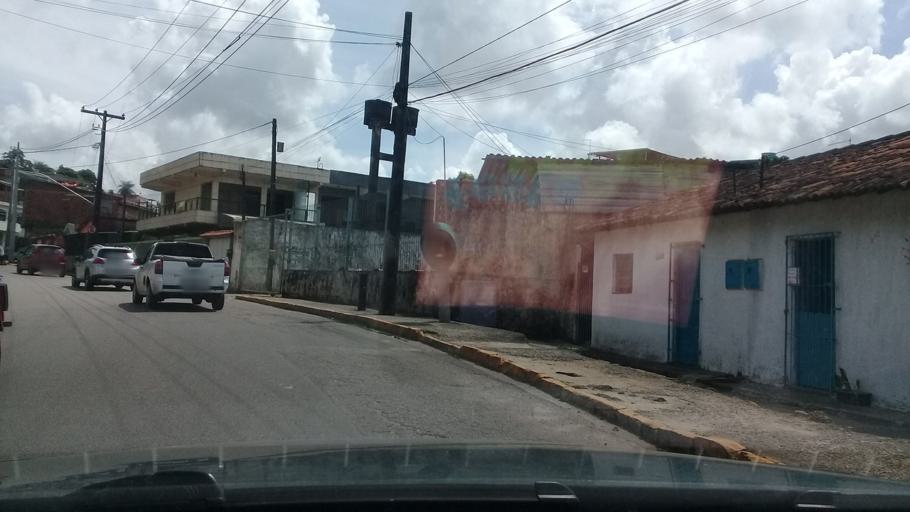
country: BR
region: Pernambuco
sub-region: Jaboatao Dos Guararapes
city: Jaboatao dos Guararapes
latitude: -8.1018
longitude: -35.0191
